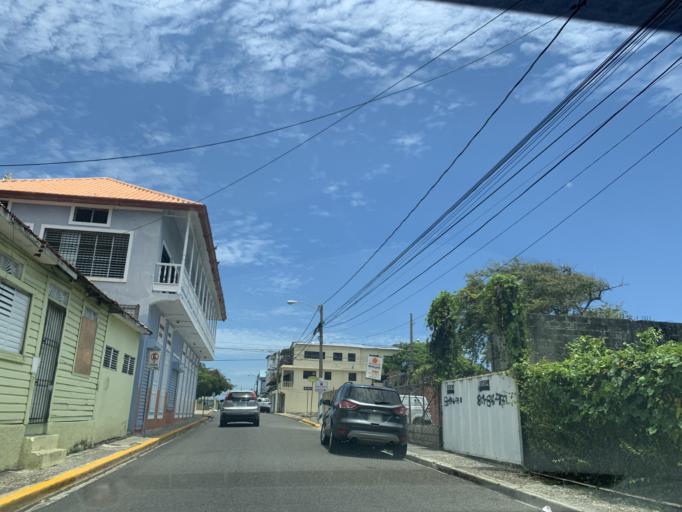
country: DO
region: Puerto Plata
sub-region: Puerto Plata
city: Puerto Plata
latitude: 19.7967
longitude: -70.6886
